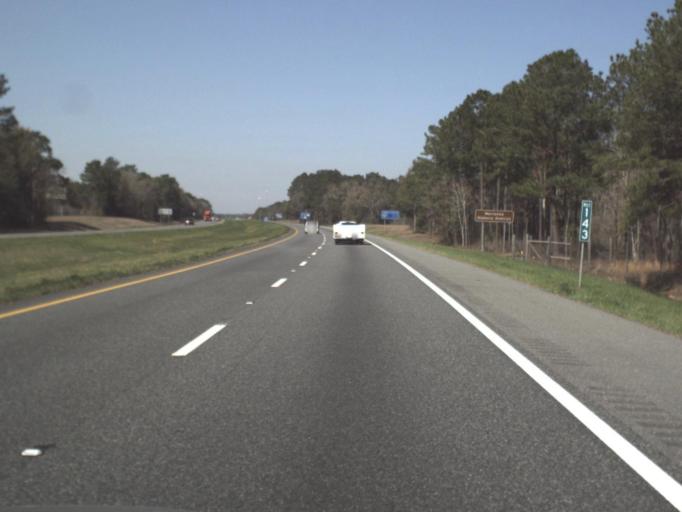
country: US
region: Florida
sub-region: Jackson County
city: Marianna
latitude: 30.7170
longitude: -85.1653
